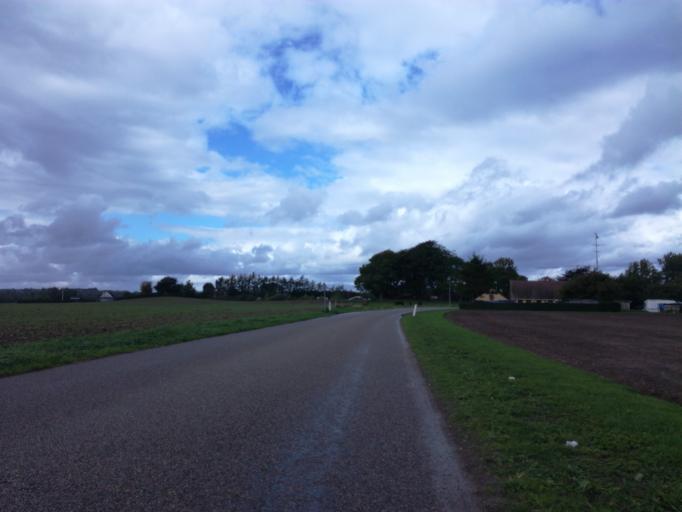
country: DK
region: South Denmark
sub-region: Fredericia Kommune
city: Fredericia
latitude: 55.6043
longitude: 9.7249
